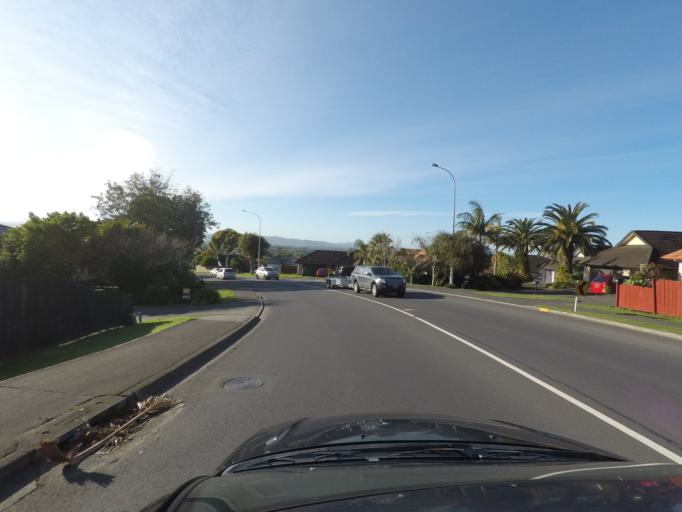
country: NZ
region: Auckland
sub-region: Auckland
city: Takanini
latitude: -37.0128
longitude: 174.9163
